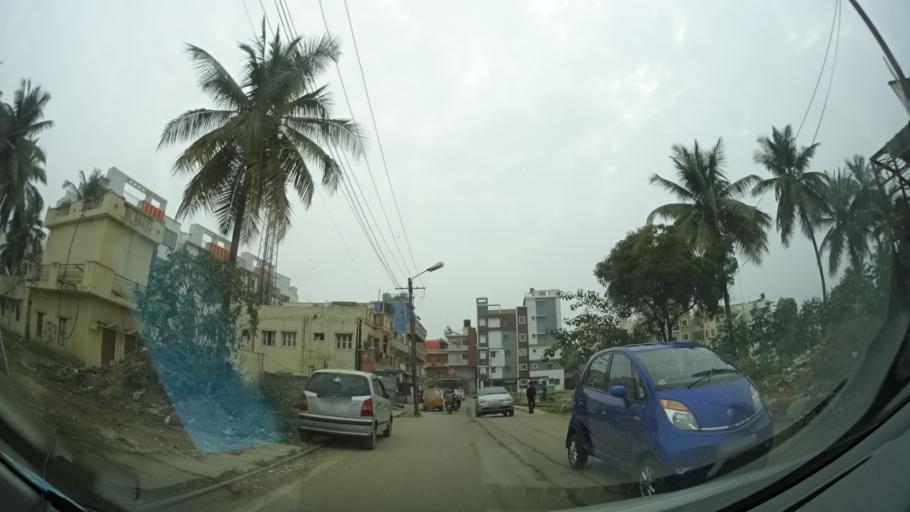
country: IN
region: Karnataka
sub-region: Bangalore Rural
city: Hoskote
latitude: 12.9782
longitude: 77.7350
